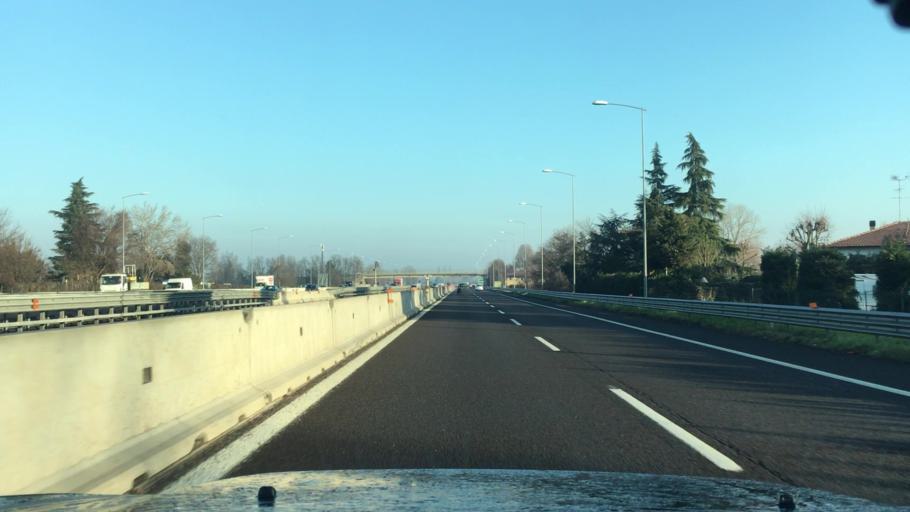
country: IT
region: Emilia-Romagna
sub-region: Provincia di Bologna
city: Casalecchio di Reno
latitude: 44.4987
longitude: 11.2718
